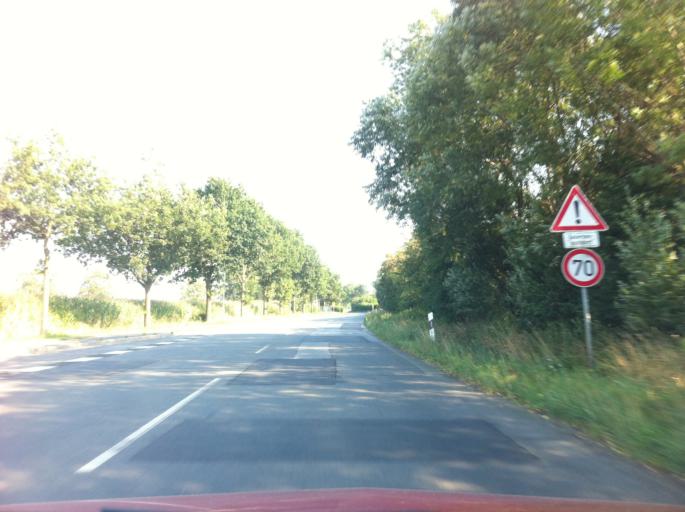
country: DE
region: Schleswig-Holstein
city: Oldenburg in Holstein
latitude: 54.3020
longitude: 10.8529
